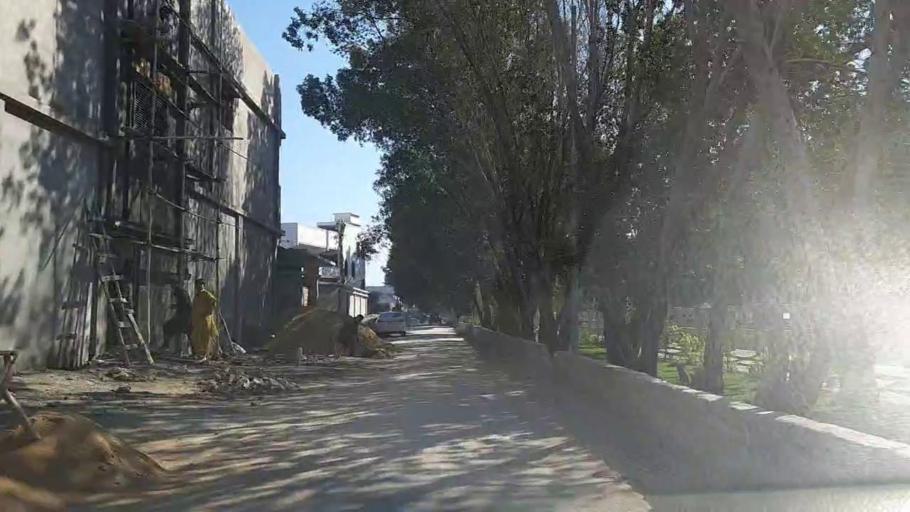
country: PK
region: Sindh
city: Nawabshah
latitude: 26.2504
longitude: 68.4202
